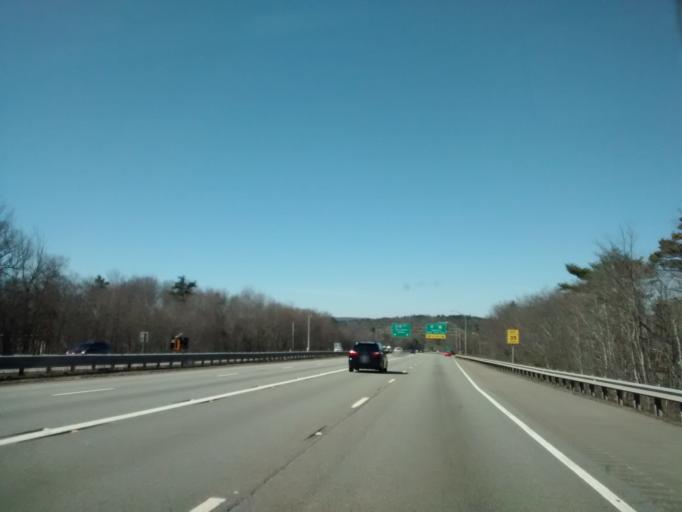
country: US
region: Massachusetts
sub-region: Worcester County
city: Sturbridge
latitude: 42.1322
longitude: -72.0522
